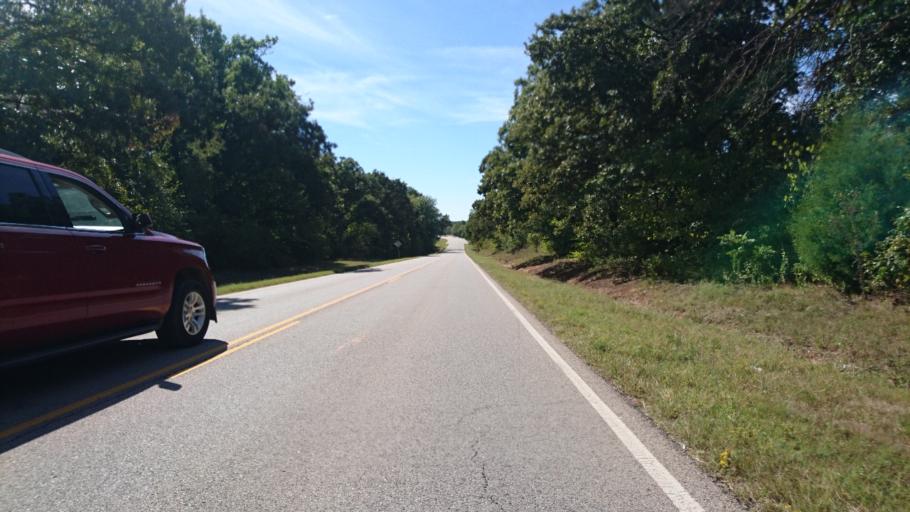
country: US
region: Oklahoma
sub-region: Lincoln County
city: Stroud
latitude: 35.7396
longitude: -96.7115
